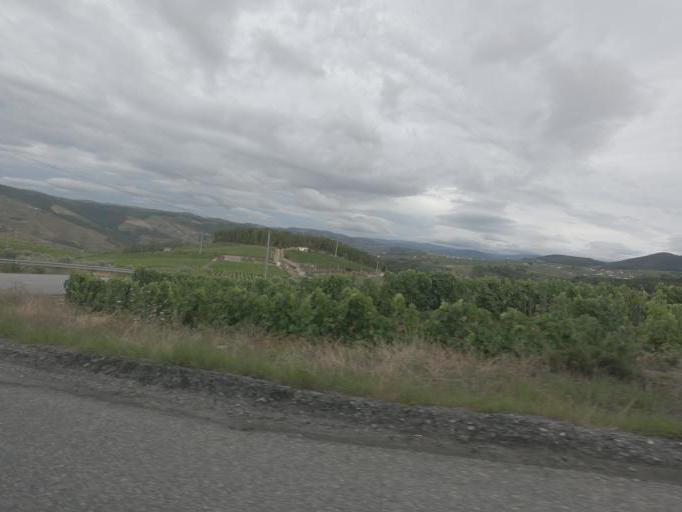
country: PT
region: Vila Real
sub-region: Sabrosa
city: Sabrosa
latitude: 41.2677
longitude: -7.5685
